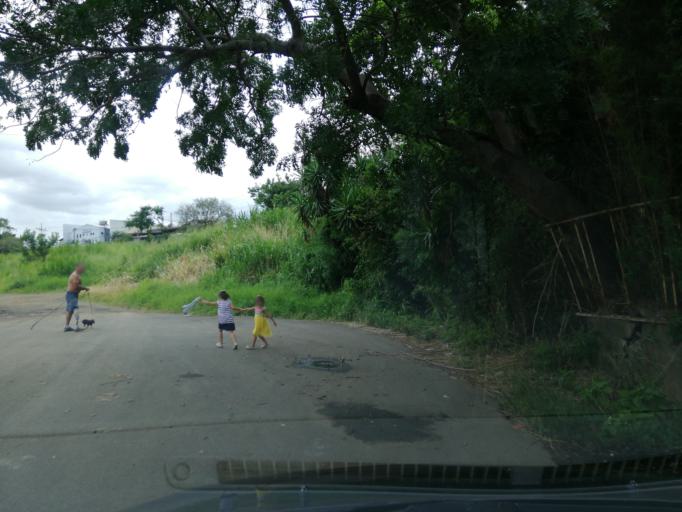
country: CR
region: Alajuela
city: Alajuela
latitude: 9.9990
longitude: -84.2103
